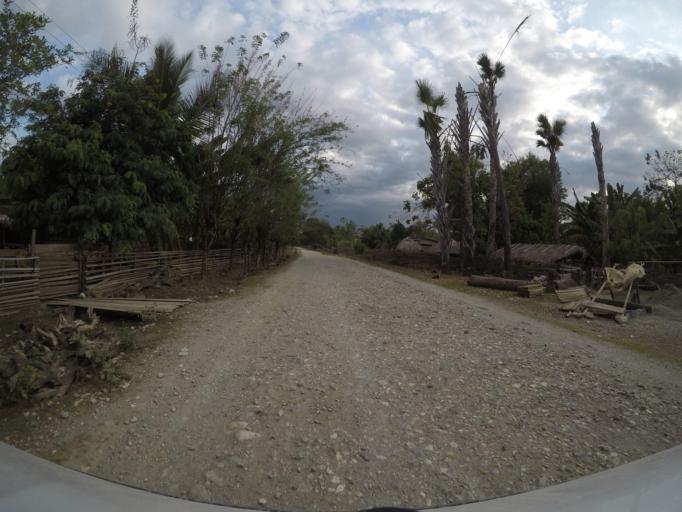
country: TL
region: Bobonaro
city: Maliana
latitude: -8.8658
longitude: 125.2146
